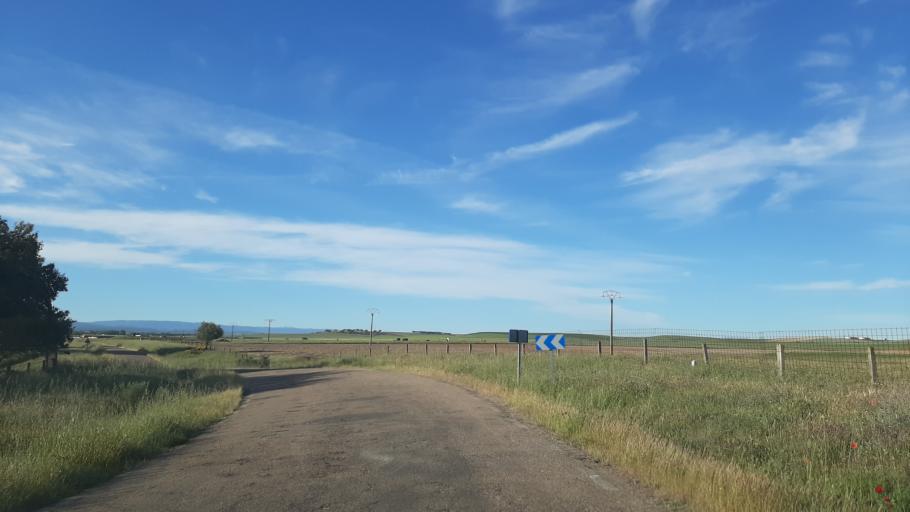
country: ES
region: Castille and Leon
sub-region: Provincia de Salamanca
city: Gajates
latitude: 40.7938
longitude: -5.3729
